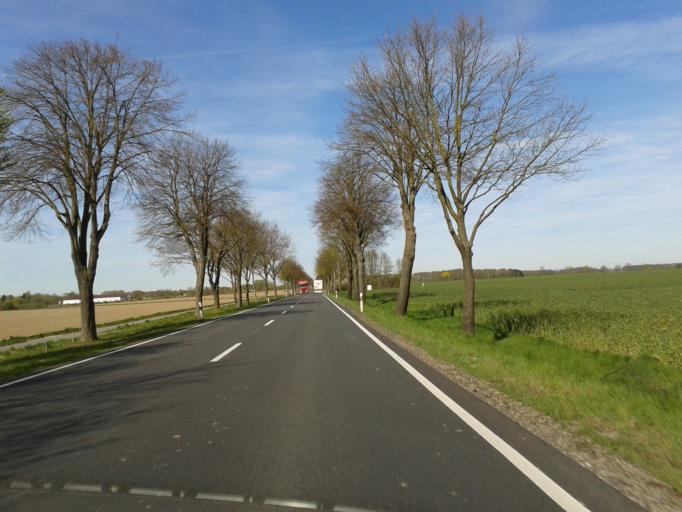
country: DE
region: Lower Saxony
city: Suhlendorf
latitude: 52.9297
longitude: 10.7865
